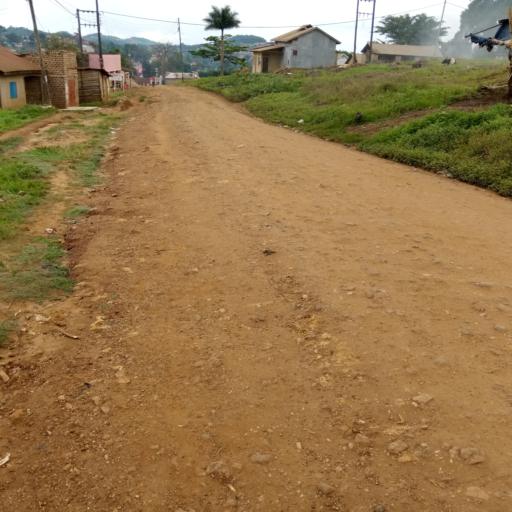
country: UG
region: Central Region
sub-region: Wakiso District
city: Wakiso
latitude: 0.4009
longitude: 32.4812
